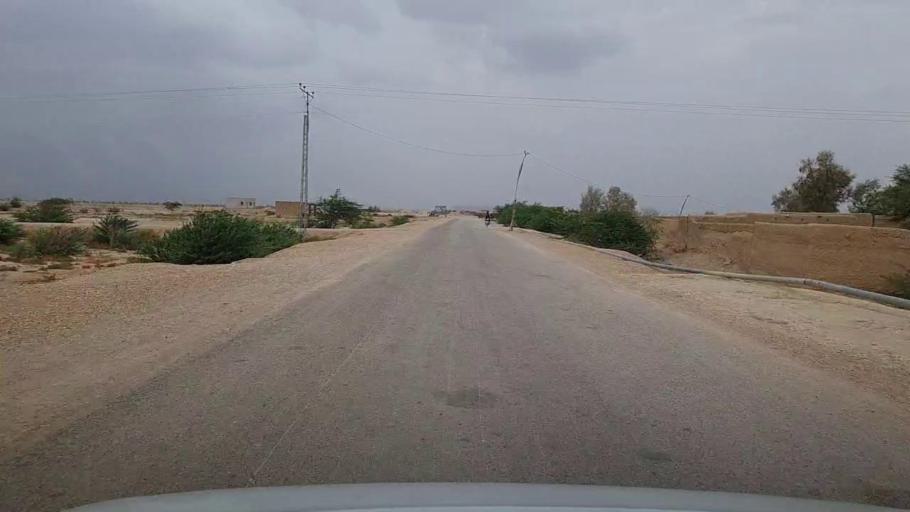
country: PK
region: Sindh
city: Sehwan
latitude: 26.3344
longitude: 67.7261
